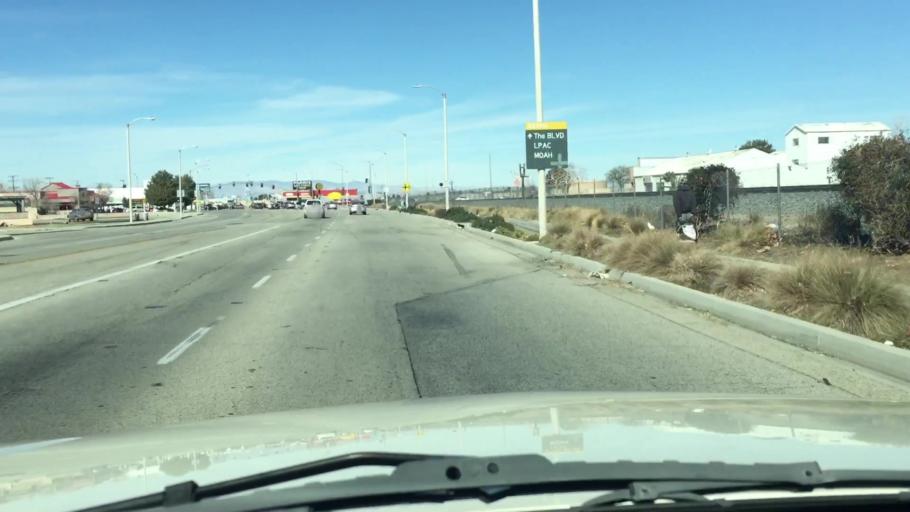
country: US
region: California
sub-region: Los Angeles County
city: Lancaster
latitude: 34.6871
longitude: -118.1347
